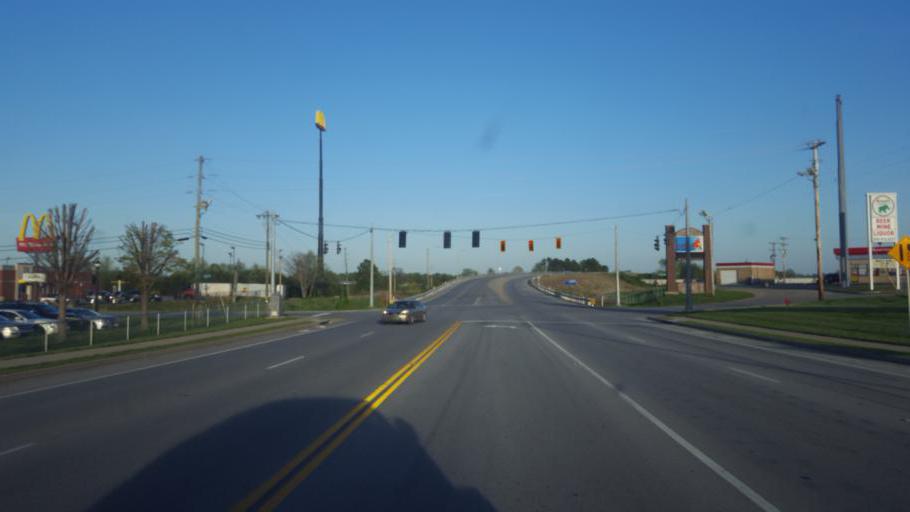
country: US
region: Kentucky
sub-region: Barren County
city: Cave City
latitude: 37.1342
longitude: -85.9728
